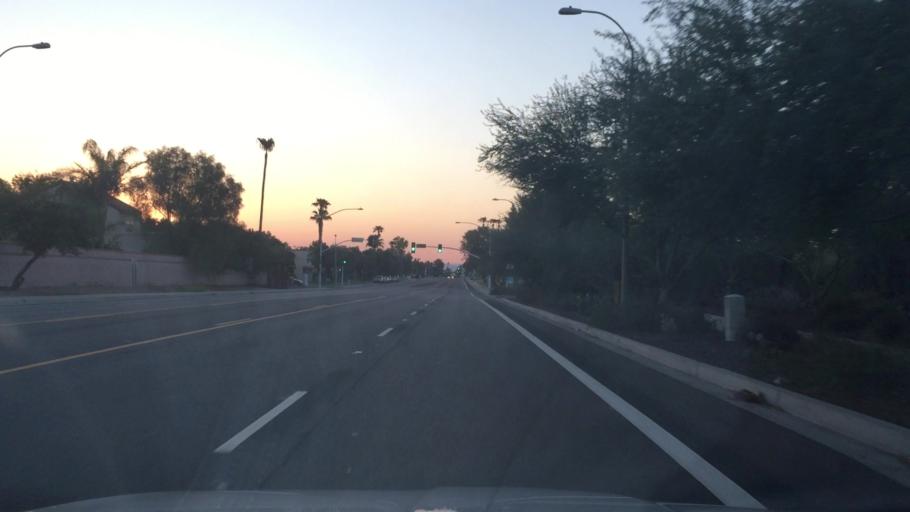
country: US
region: Arizona
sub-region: Maricopa County
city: Scottsdale
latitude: 33.5238
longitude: -111.9059
